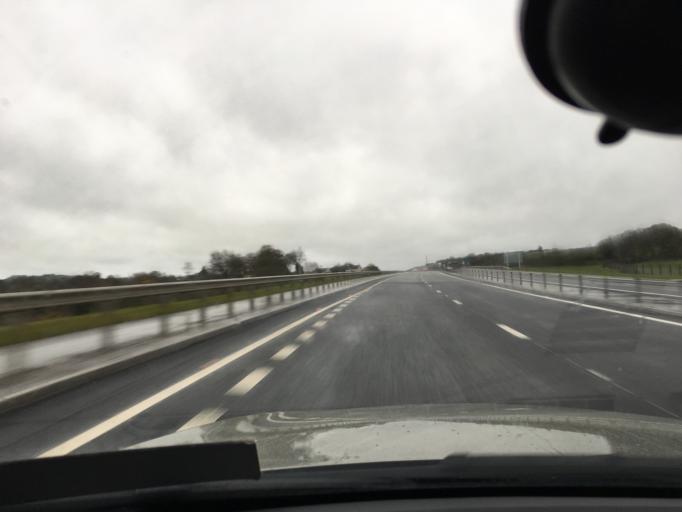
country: GB
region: Northern Ireland
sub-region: Larne District
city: Larne
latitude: 54.8138
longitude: -5.9003
